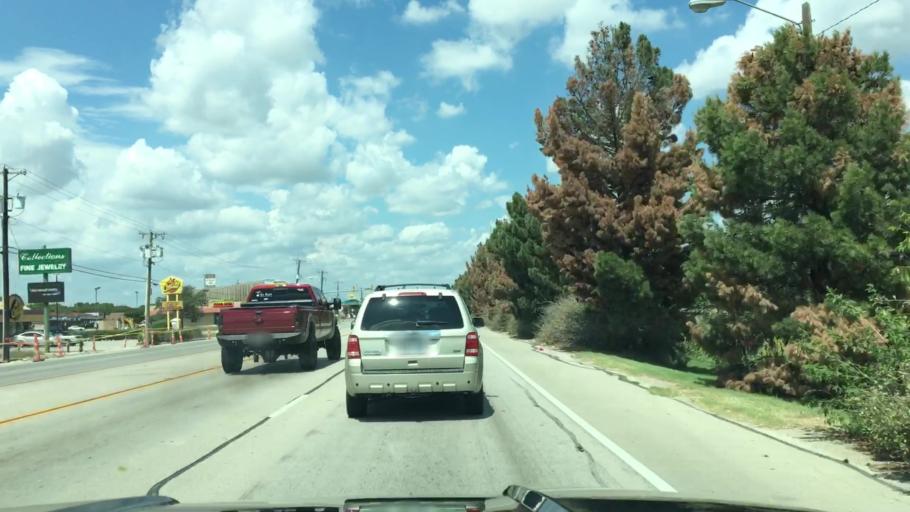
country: US
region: Texas
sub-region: Tarrant County
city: Saginaw
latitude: 32.8521
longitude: -97.3606
